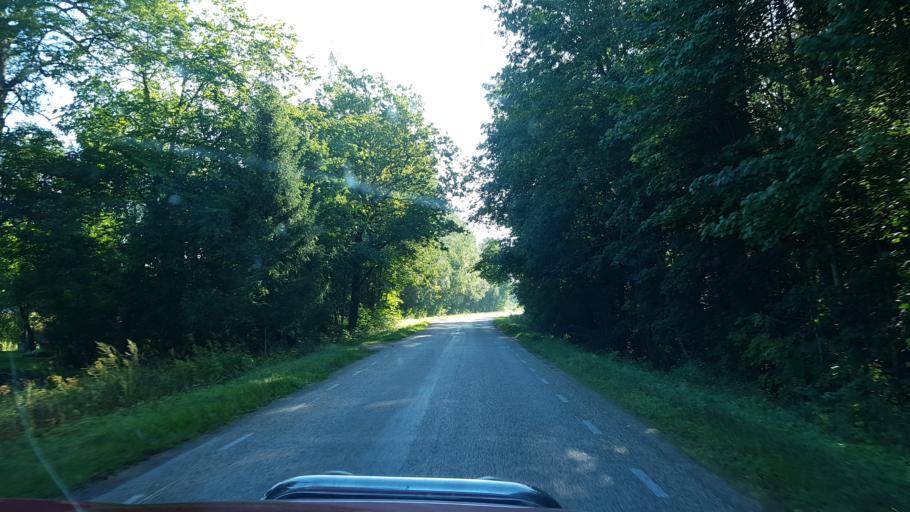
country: EE
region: Jogevamaa
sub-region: Tabivere vald
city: Tabivere
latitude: 58.6687
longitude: 26.7744
